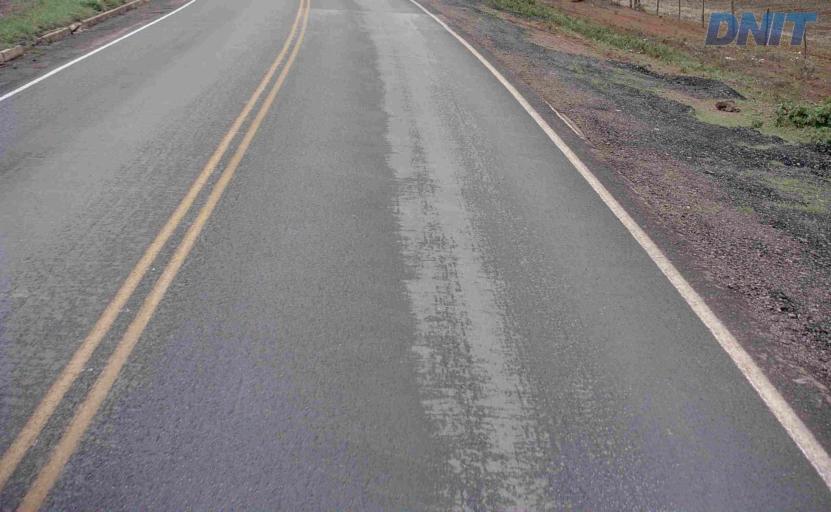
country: BR
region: Goias
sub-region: Padre Bernardo
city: Padre Bernardo
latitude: -15.2783
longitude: -48.2603
